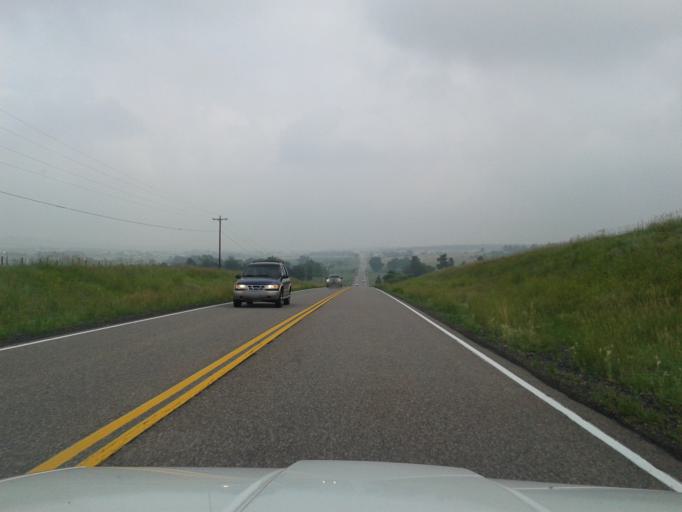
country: US
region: Colorado
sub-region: Douglas County
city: The Pinery
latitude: 39.3672
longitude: -104.7484
